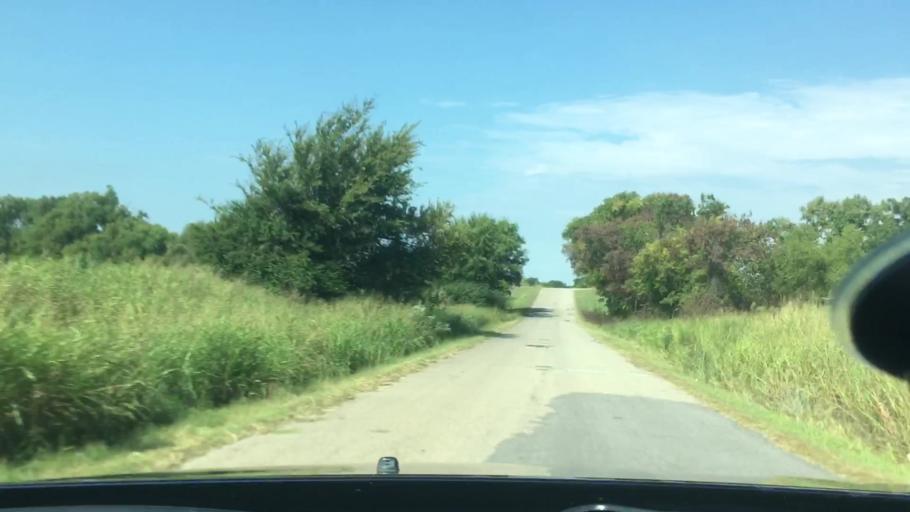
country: US
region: Oklahoma
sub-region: Bryan County
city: Calera
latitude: 33.9110
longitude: -96.4618
